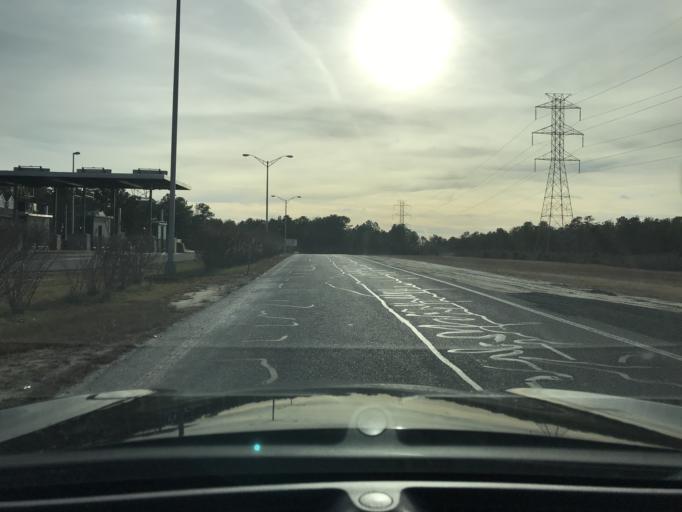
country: US
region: New Jersey
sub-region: Ocean County
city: Forked River
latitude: 39.8638
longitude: -74.2217
